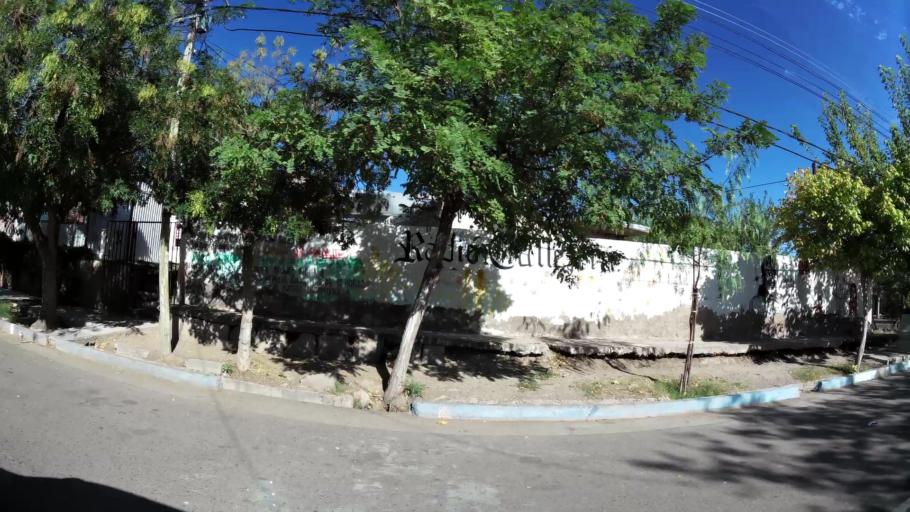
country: AR
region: Mendoza
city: Mendoza
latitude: -32.8737
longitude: -68.8691
